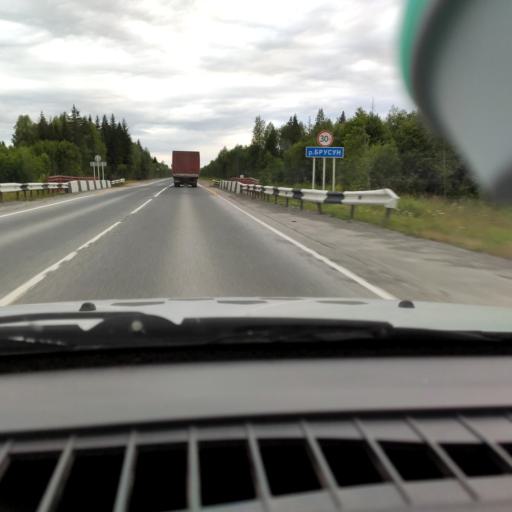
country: RU
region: Perm
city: Kalino
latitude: 58.3154
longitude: 57.5826
